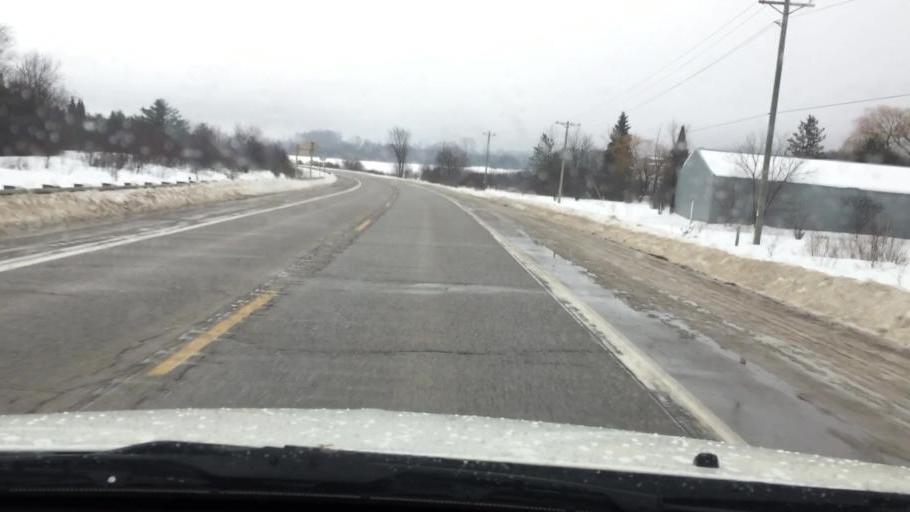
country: US
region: Michigan
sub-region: Charlevoix County
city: East Jordan
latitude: 45.1313
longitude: -85.1391
